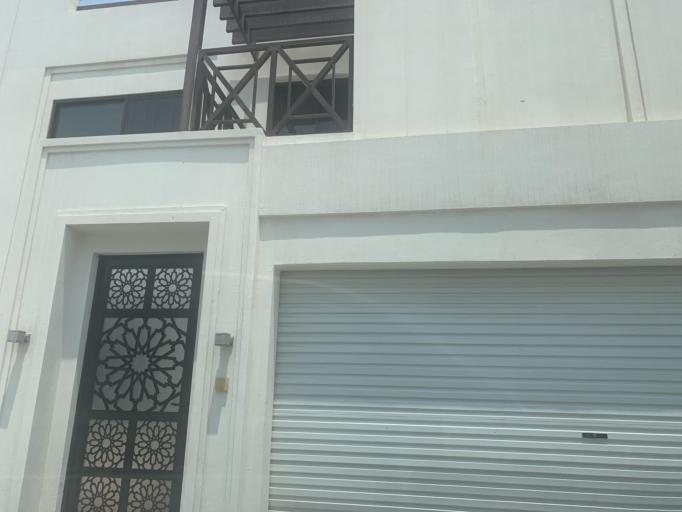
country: BH
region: Muharraq
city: Al Muharraq
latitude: 26.3147
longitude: 50.6244
